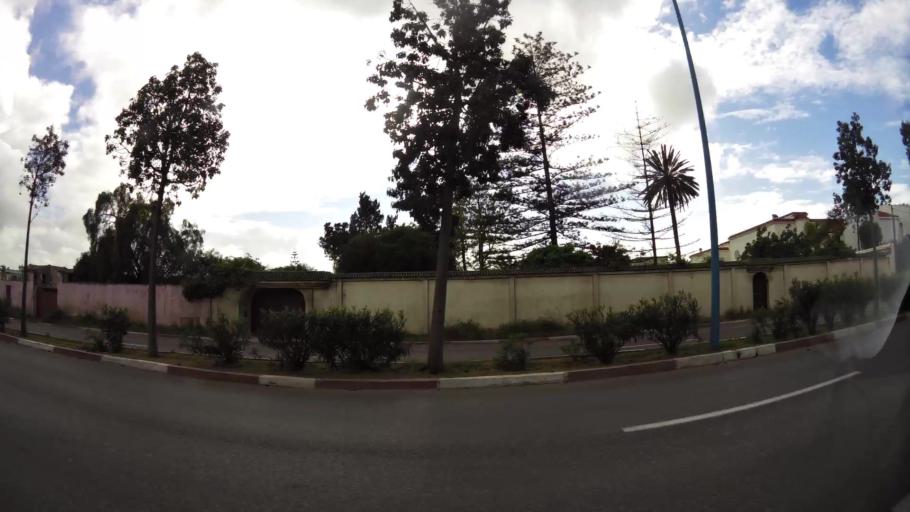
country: MA
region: Grand Casablanca
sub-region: Casablanca
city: Casablanca
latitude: 33.5455
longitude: -7.6212
